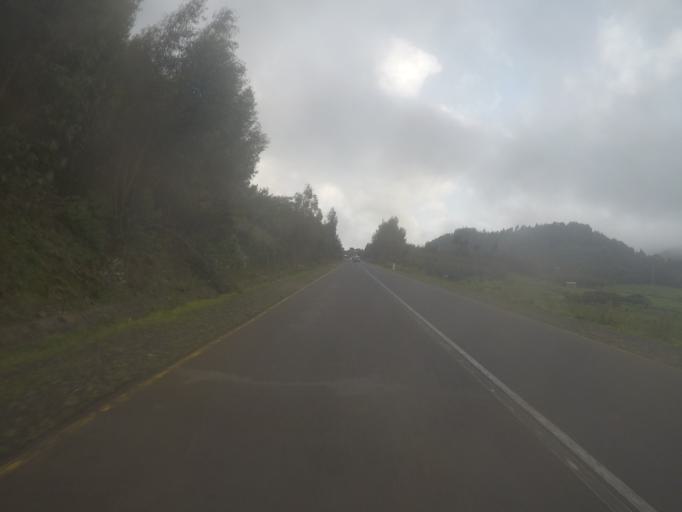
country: ET
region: Amhara
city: Gondar
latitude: 12.7236
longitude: 37.5074
